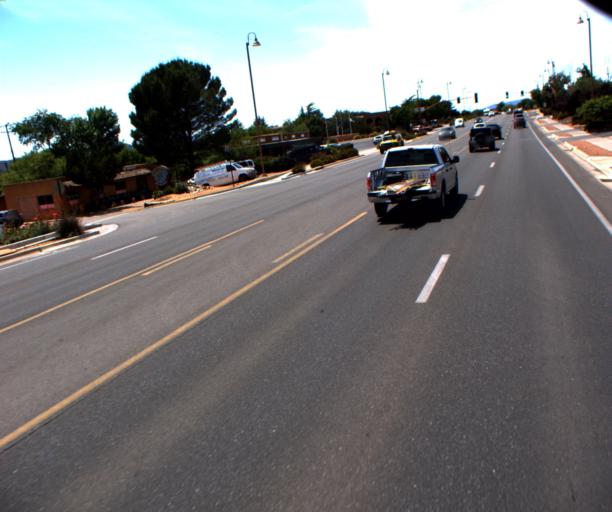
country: US
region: Arizona
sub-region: Yavapai County
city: West Sedona
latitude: 34.8634
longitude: -111.7891
